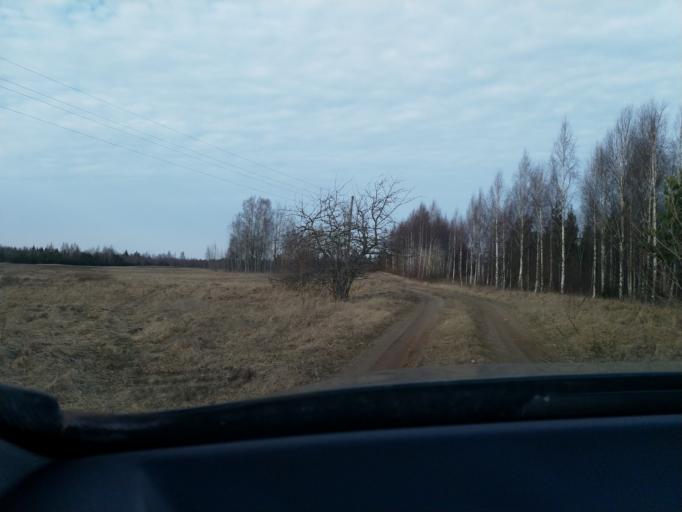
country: LV
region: Kuldigas Rajons
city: Kuldiga
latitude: 57.0426
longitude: 21.8550
